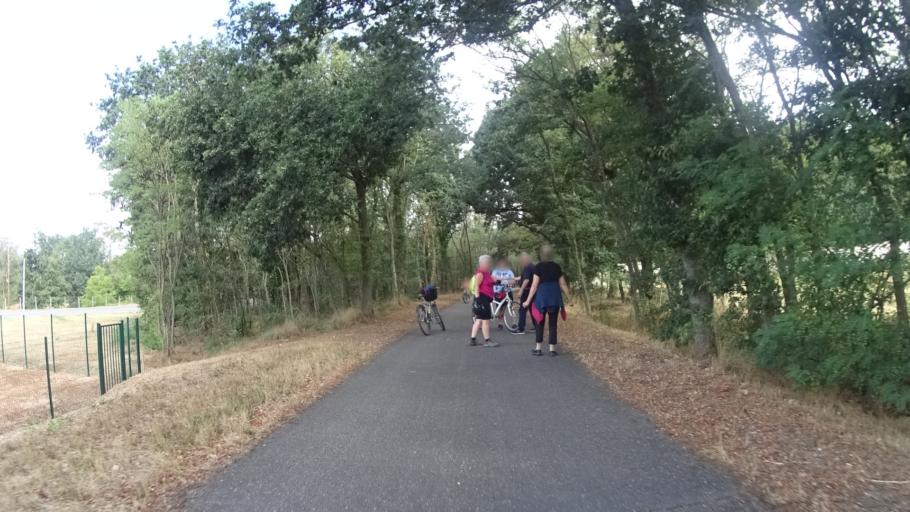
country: FR
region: Auvergne
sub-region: Departement de l'Allier
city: Diou
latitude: 46.5724
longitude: 3.7463
